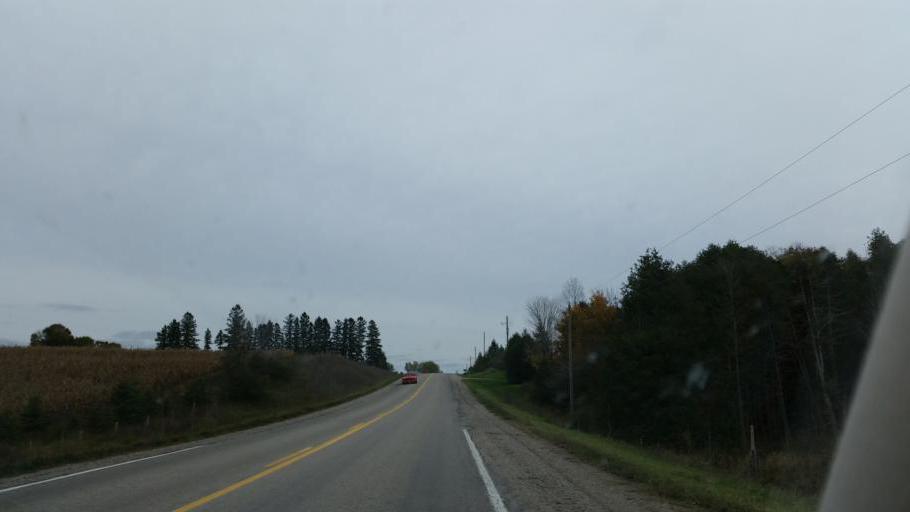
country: CA
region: Ontario
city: Wingham
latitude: 43.9939
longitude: -81.3340
